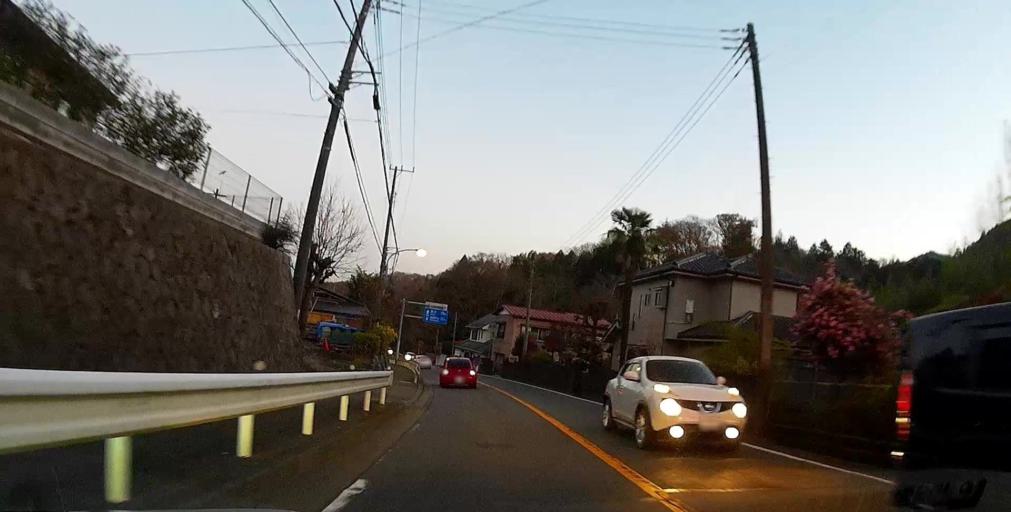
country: JP
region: Yamanashi
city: Uenohara
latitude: 35.6007
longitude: 139.2002
